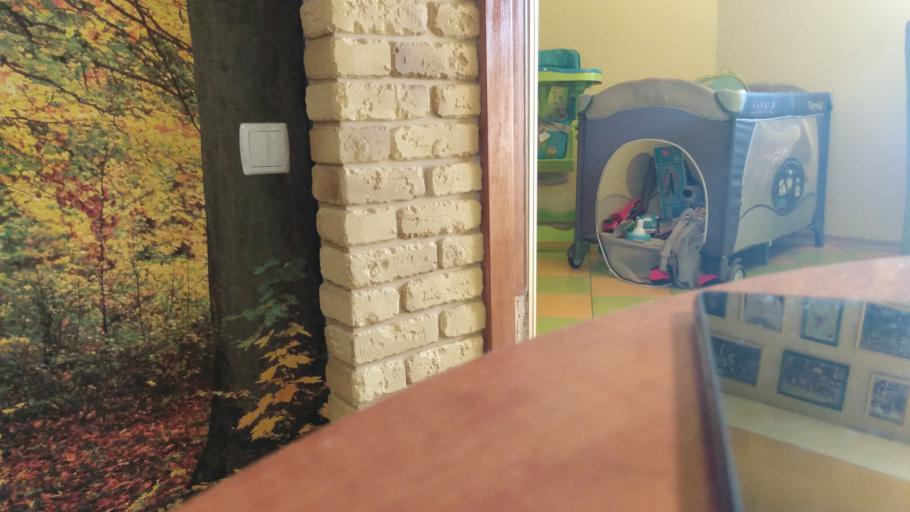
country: RU
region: Tverskaya
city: Bologoye
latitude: 57.9369
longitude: 34.1894
